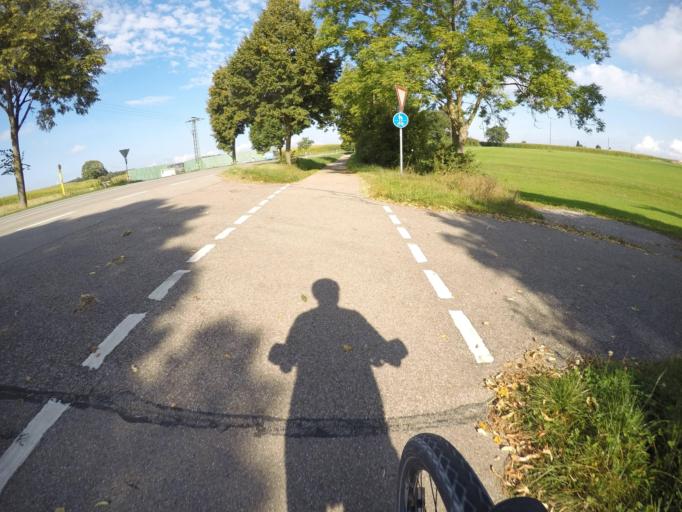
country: DE
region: Bavaria
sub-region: Swabia
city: Ehingen
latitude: 48.6057
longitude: 10.8068
